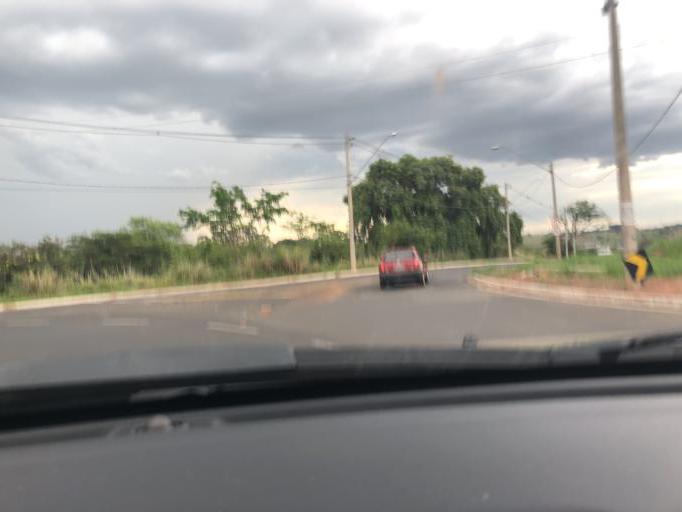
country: BR
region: Sao Paulo
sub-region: Sao Jose Do Rio Preto
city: Sao Jose do Rio Preto
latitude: -20.8305
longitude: -49.4263
